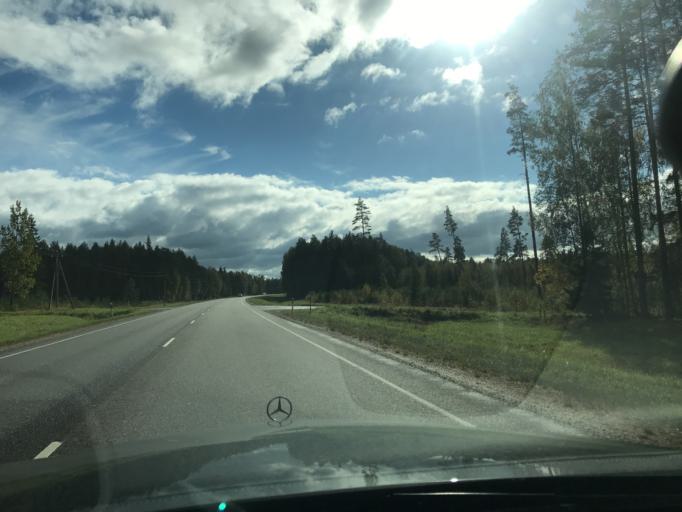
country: EE
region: Vorumaa
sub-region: Voru linn
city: Voru
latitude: 57.8390
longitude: 27.0557
